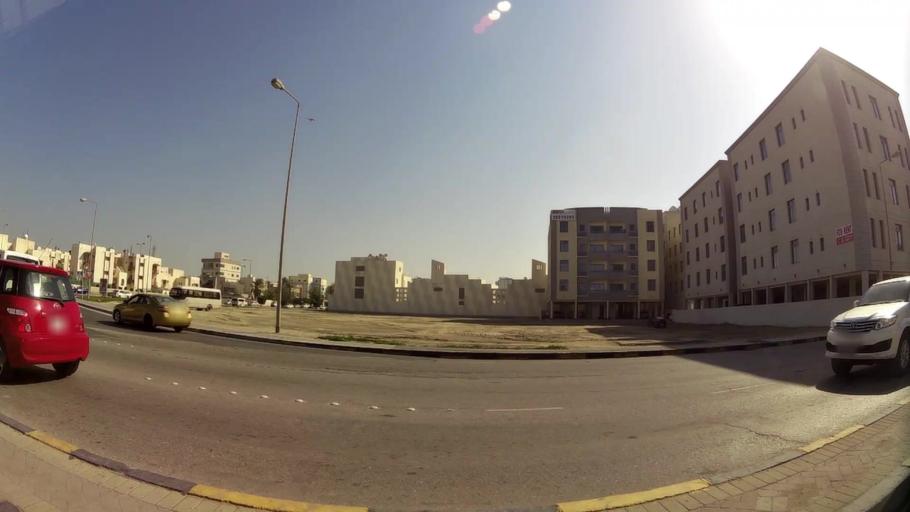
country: BH
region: Manama
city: Manama
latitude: 26.2188
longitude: 50.5790
